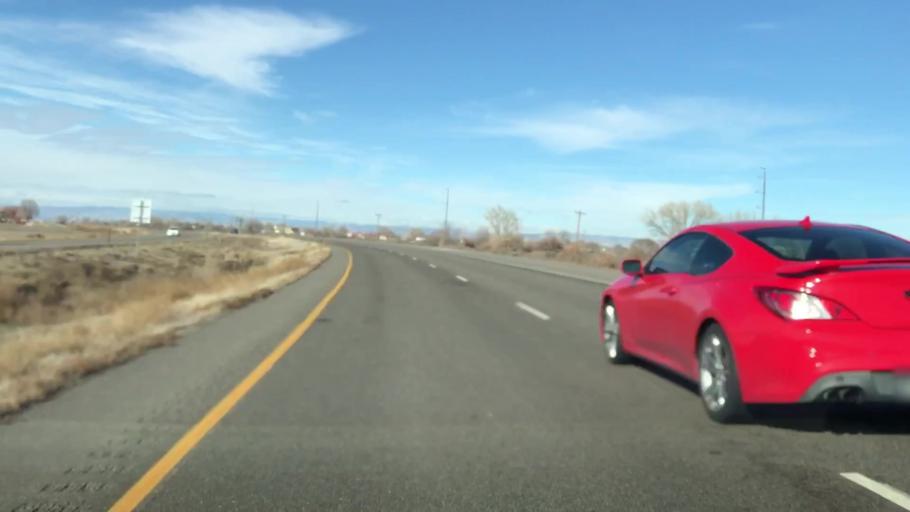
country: US
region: Colorado
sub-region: Mesa County
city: Fruita
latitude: 39.1284
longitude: -108.6840
